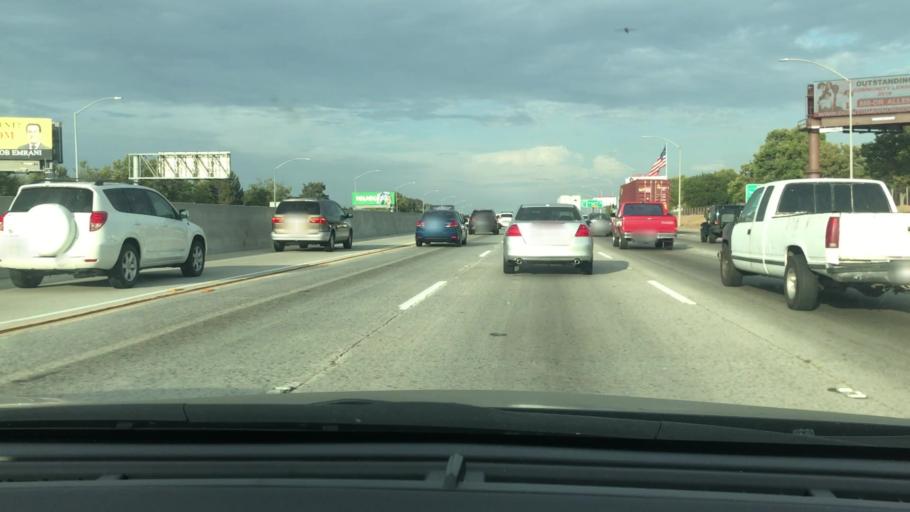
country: US
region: California
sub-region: Los Angeles County
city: West Rancho Dominguez
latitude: 33.8730
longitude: -118.2448
